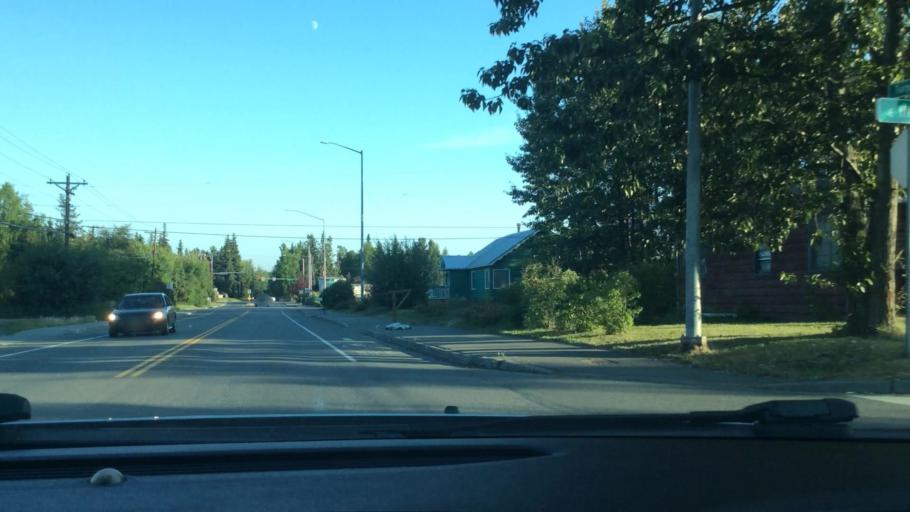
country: US
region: Alaska
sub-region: Anchorage Municipality
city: Elmendorf Air Force Base
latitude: 61.2118
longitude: -149.7559
